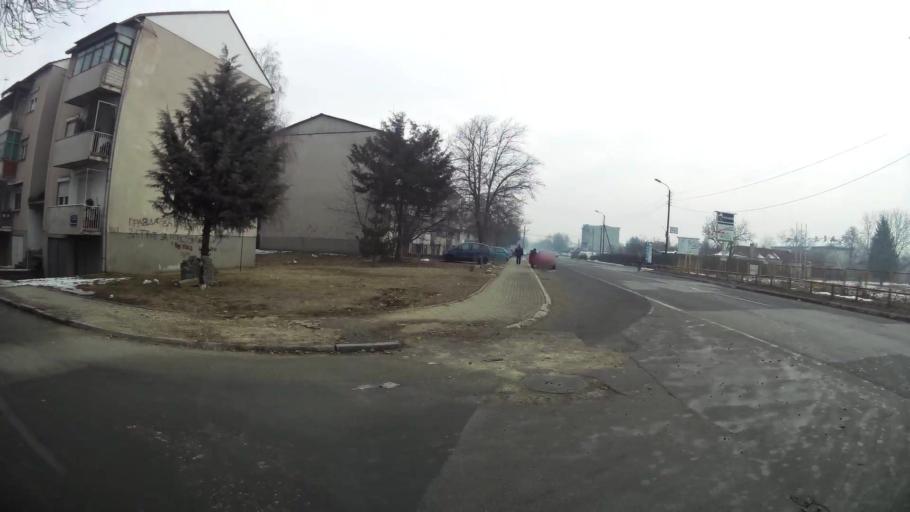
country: MK
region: Kisela Voda
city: Kisela Voda
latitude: 41.9982
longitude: 21.4927
